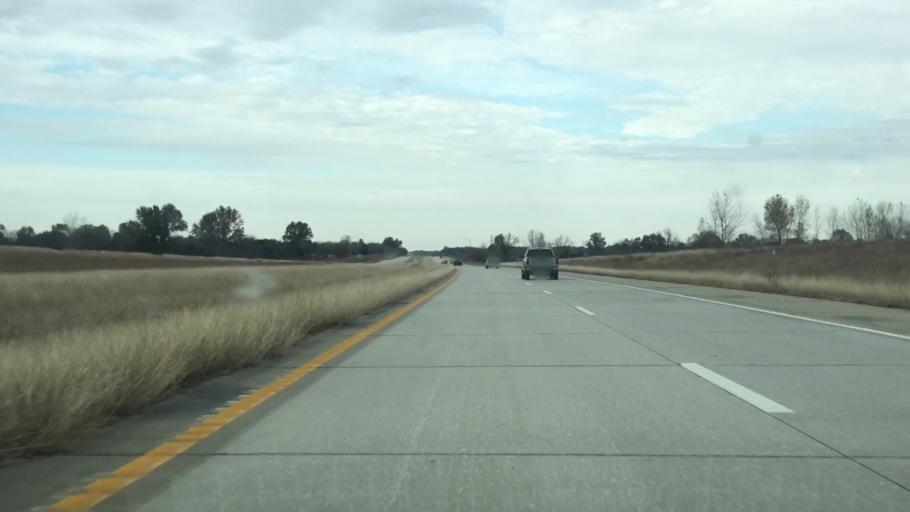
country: US
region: Missouri
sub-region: Henry County
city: Clinton
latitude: 38.2505
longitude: -93.7611
